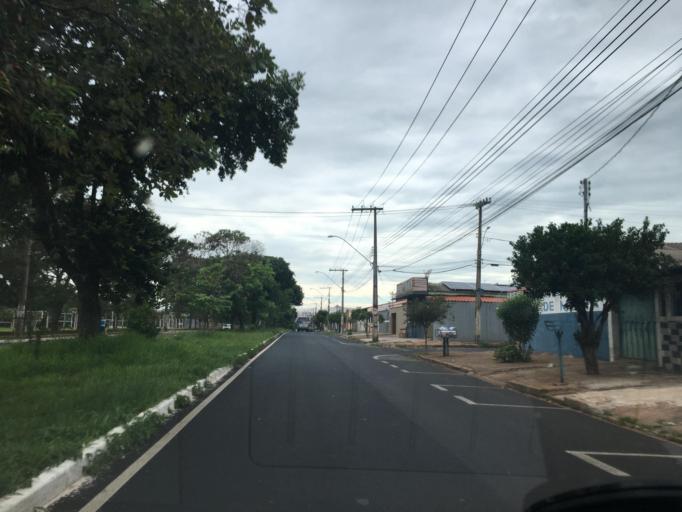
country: BR
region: Minas Gerais
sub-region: Uberlandia
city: Uberlandia
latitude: -18.9278
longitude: -48.3114
